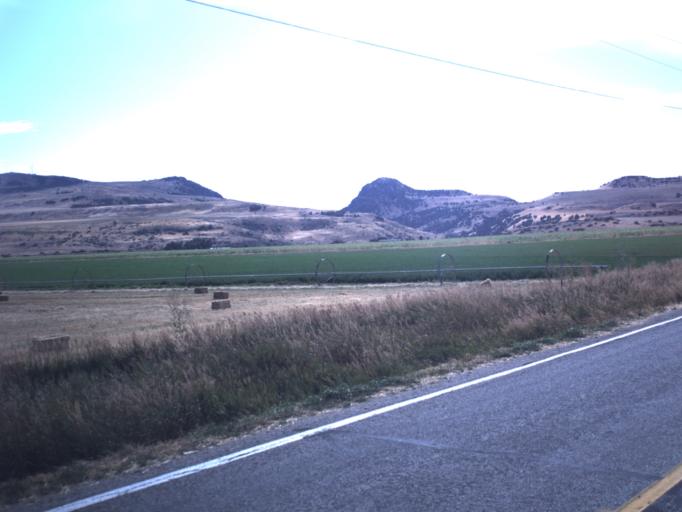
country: US
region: Utah
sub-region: Cache County
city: Benson
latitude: 41.8627
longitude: -112.0026
